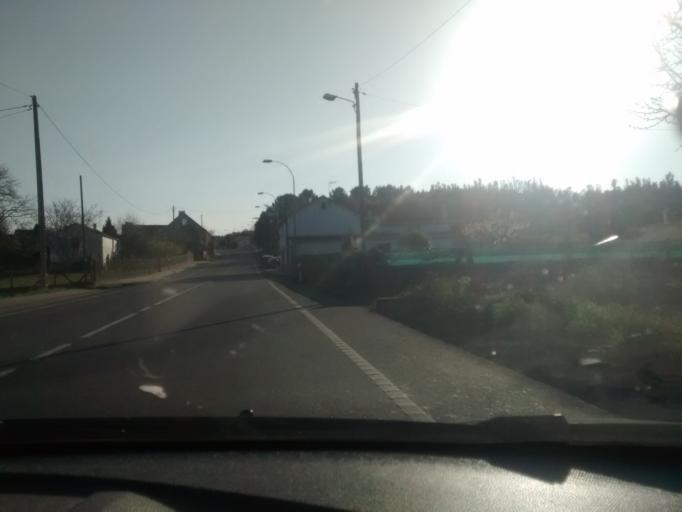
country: ES
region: Galicia
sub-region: Provincia de Pontevedra
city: A Estrada
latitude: 42.6953
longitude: -8.4640
